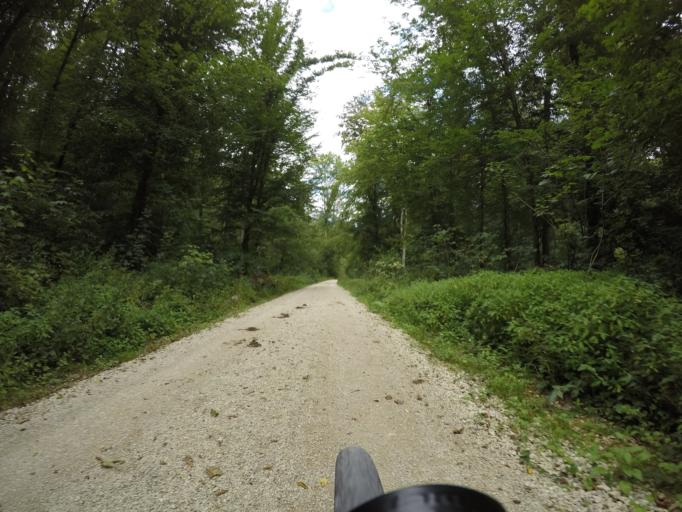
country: DE
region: Baden-Wuerttemberg
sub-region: Tuebingen Region
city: Reutlingen
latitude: 48.4569
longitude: 9.1691
